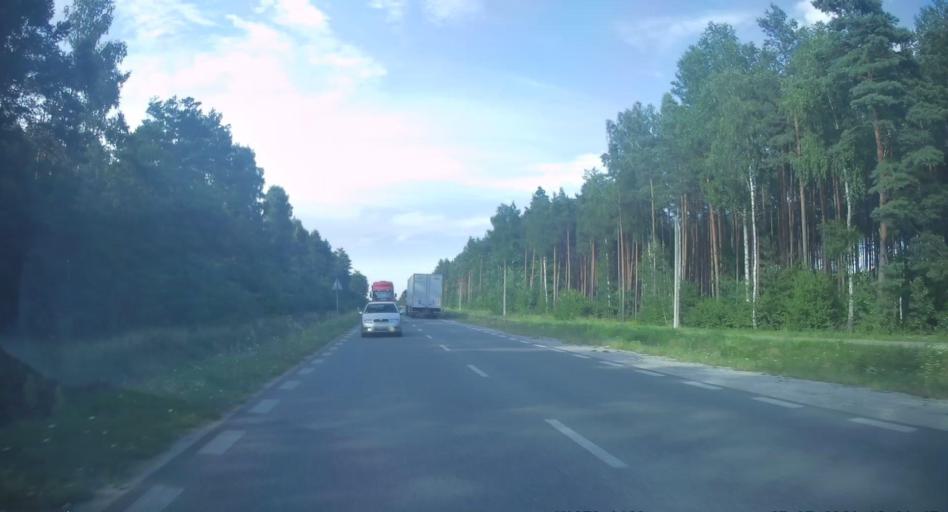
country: PL
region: Swietokrzyskie
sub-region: Powiat konecki
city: Konskie
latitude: 51.1240
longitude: 20.3563
